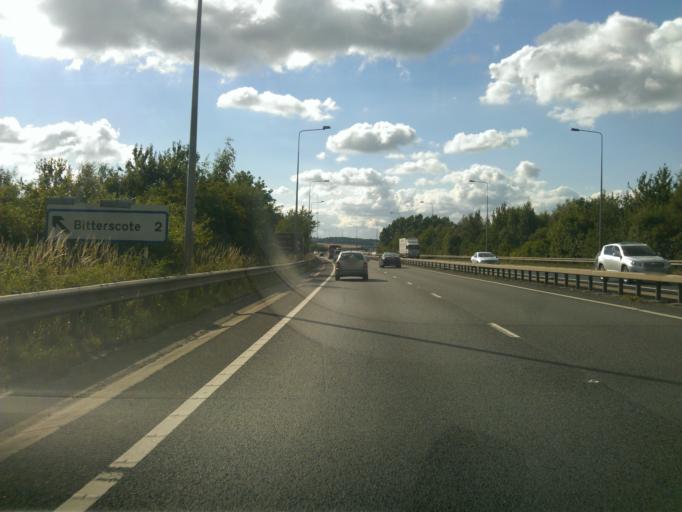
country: GB
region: England
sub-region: Staffordshire
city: Fazeley
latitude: 52.6234
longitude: -1.6919
